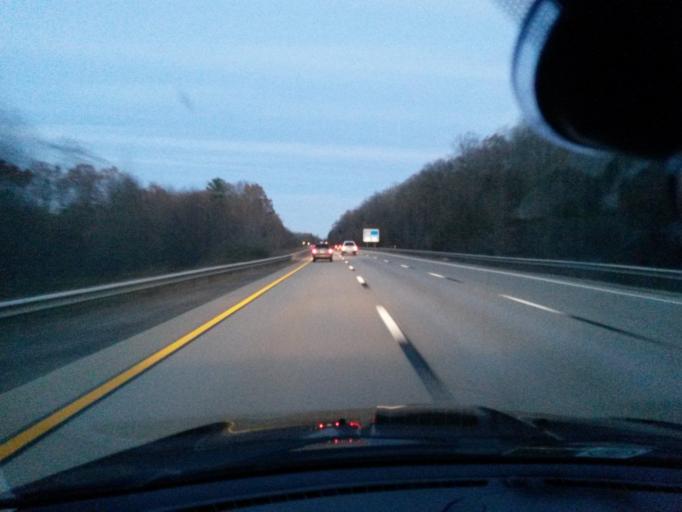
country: US
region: West Virginia
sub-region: Raleigh County
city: Daniels
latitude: 37.7721
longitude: -81.1035
